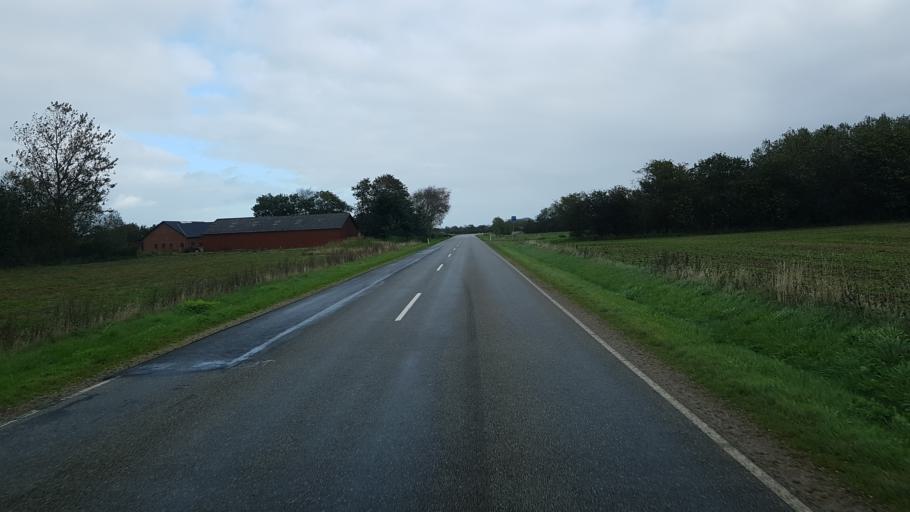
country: DK
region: South Denmark
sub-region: Billund Kommune
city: Grindsted
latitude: 55.7609
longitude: 8.7730
